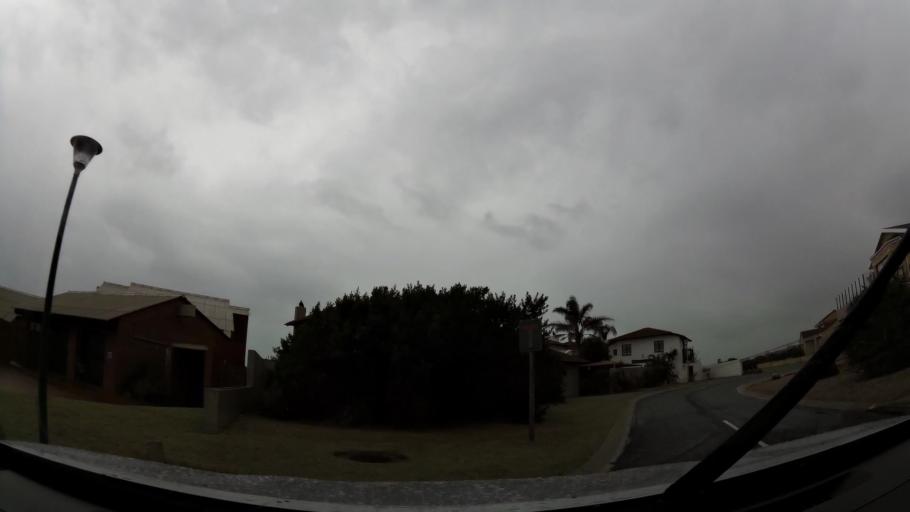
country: ZA
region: Western Cape
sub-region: Eden District Municipality
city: Mossel Bay
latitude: -34.0478
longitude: 22.2839
